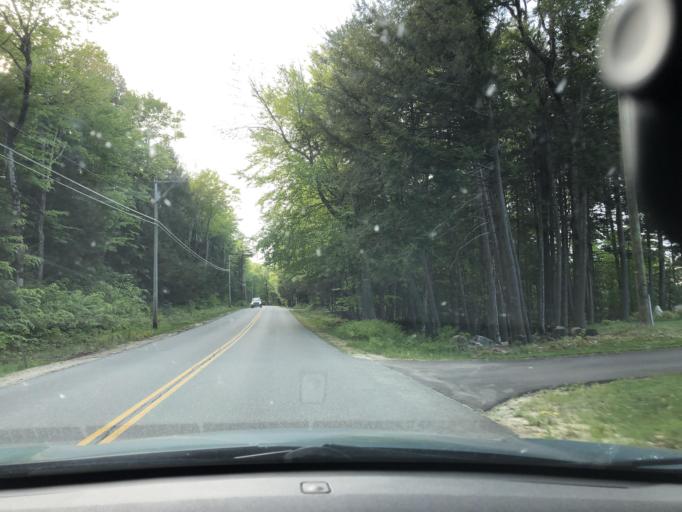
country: US
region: New Hampshire
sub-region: Merrimack County
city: New London
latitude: 43.4093
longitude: -71.9607
